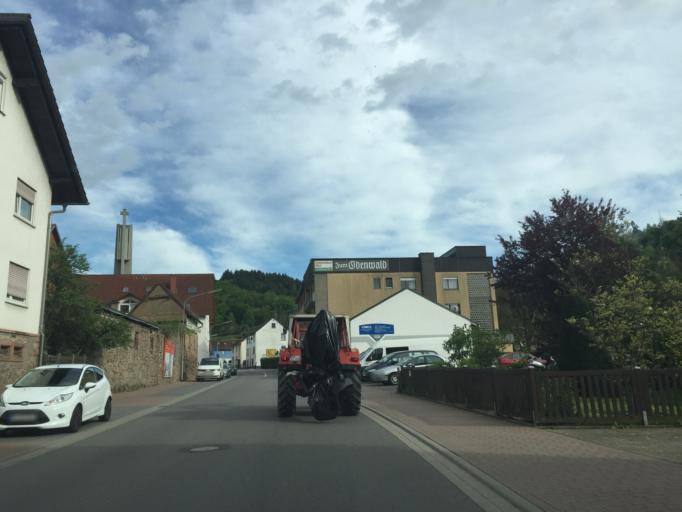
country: DE
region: Hesse
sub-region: Regierungsbezirk Darmstadt
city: Birkenau
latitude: 49.5323
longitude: 8.7286
